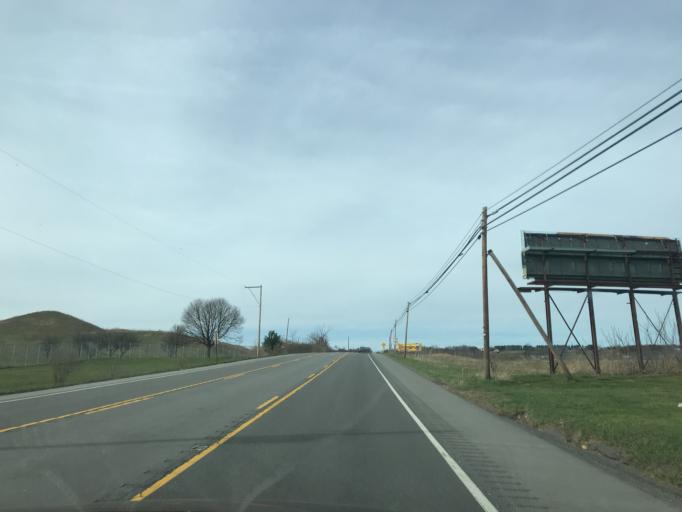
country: US
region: Pennsylvania
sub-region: Lycoming County
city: Montgomery
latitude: 41.1461
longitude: -76.9124
